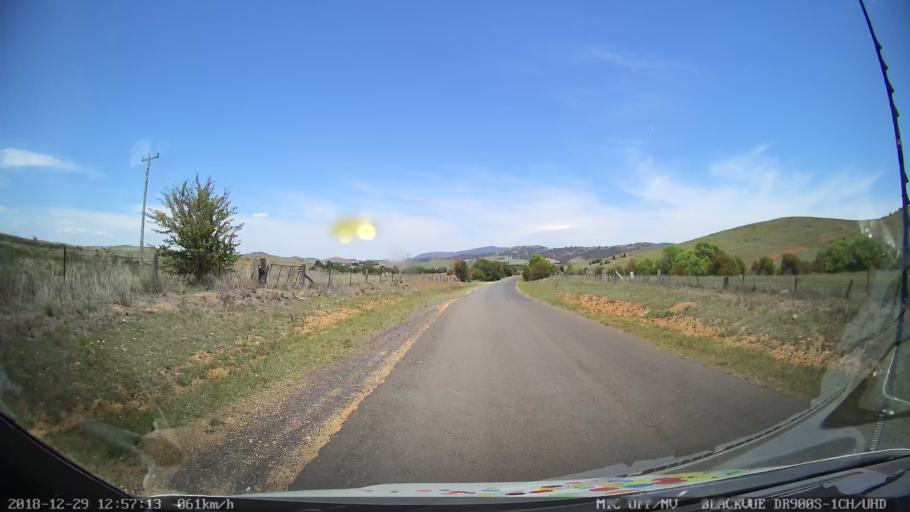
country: AU
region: Australian Capital Territory
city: Macarthur
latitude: -35.7064
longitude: 149.1790
